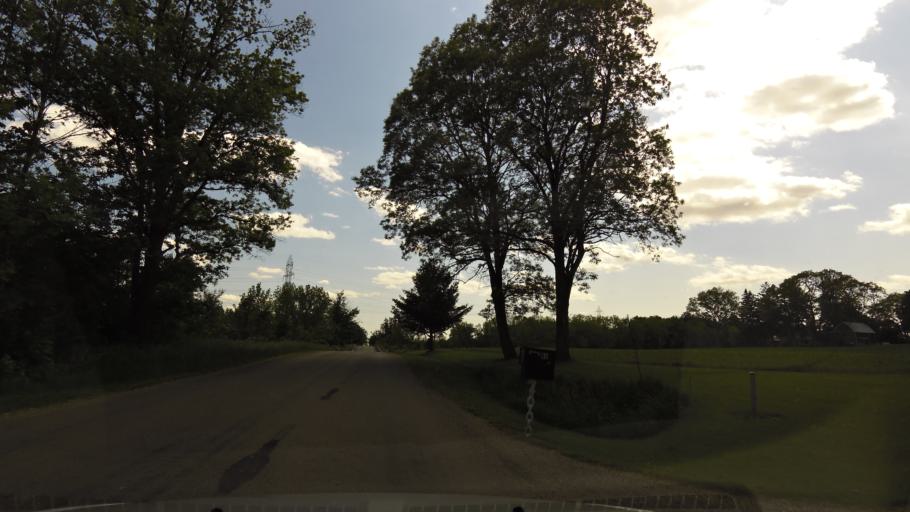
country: CA
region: Ontario
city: Ancaster
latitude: 43.1293
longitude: -80.0811
